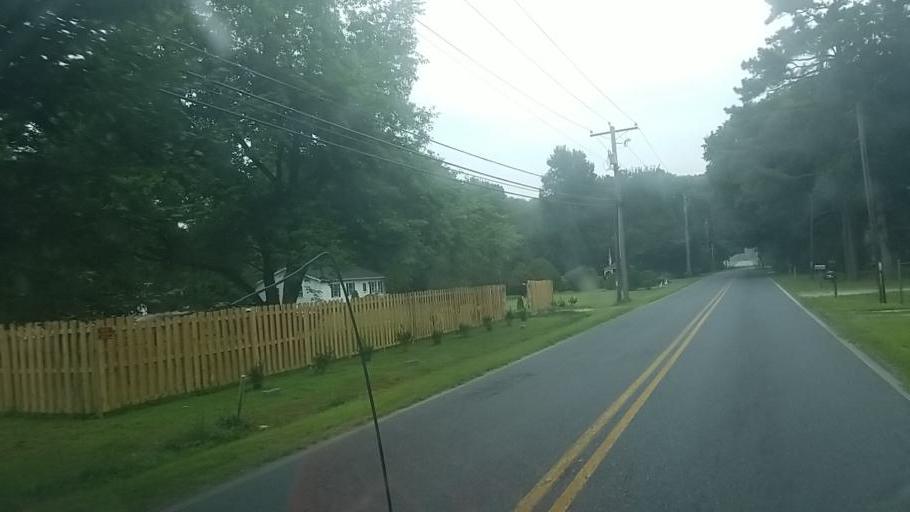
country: US
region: Maryland
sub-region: Wicomico County
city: Salisbury
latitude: 38.3785
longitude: -75.5246
